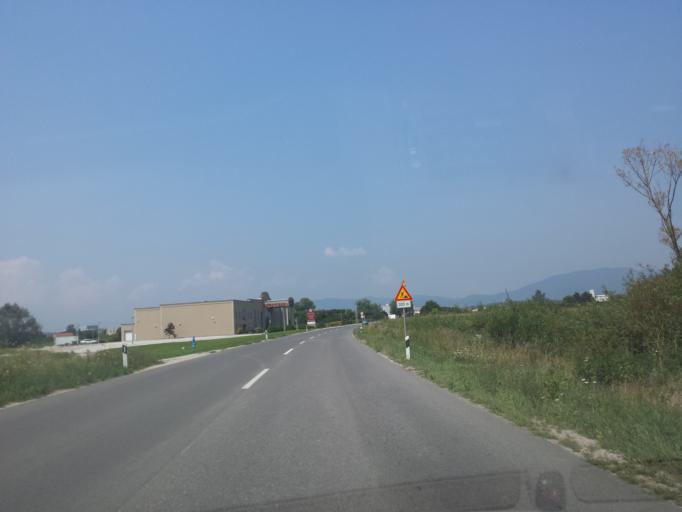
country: HR
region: Zagrebacka
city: Jastrebarsko
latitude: 45.6533
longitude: 15.6576
